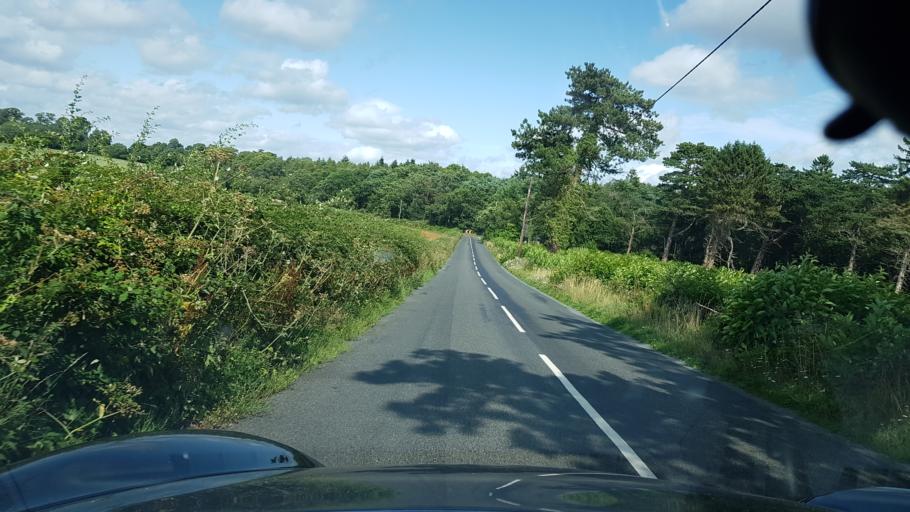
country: GB
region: England
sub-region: Surrey
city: Seale
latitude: 51.2158
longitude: -0.7170
